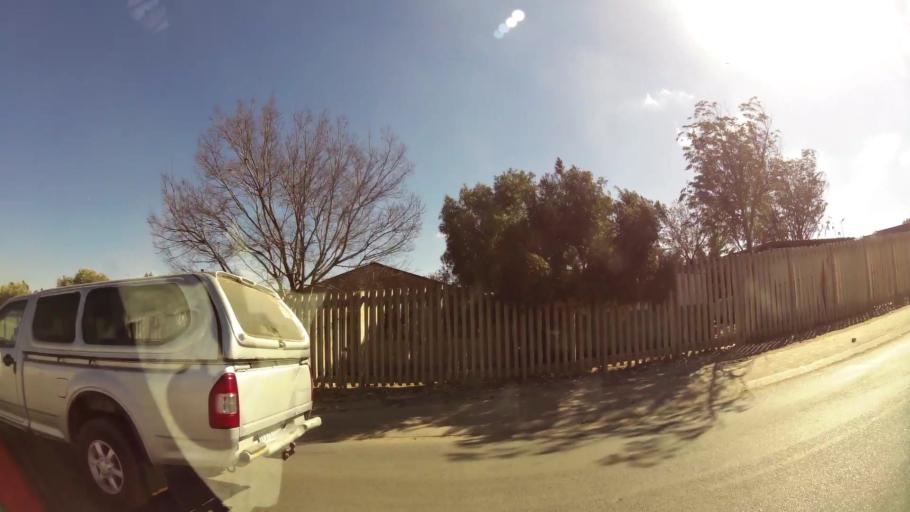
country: ZA
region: Gauteng
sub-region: City of Johannesburg Metropolitan Municipality
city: Modderfontein
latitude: -26.0341
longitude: 28.1636
